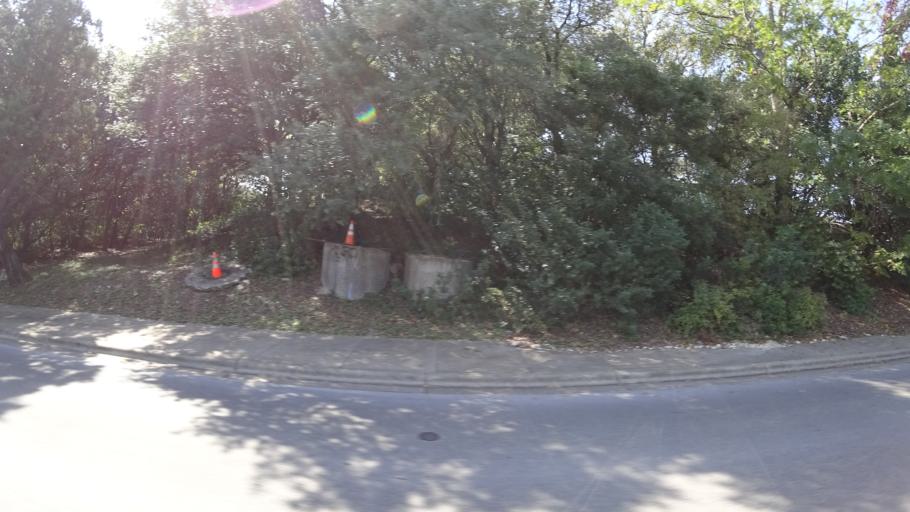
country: US
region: Texas
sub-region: Travis County
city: West Lake Hills
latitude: 30.3428
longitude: -97.7707
